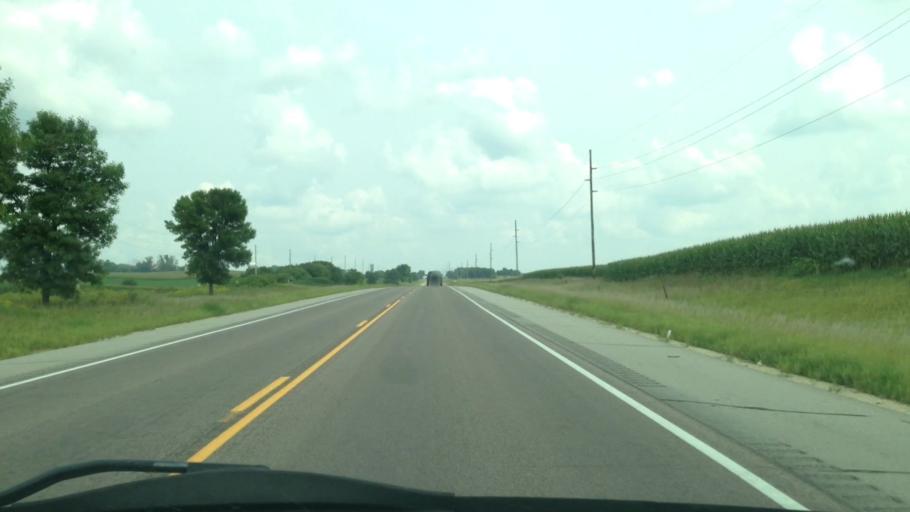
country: US
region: Minnesota
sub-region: Wabasha County
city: Elgin
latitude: 44.1420
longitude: -92.2333
